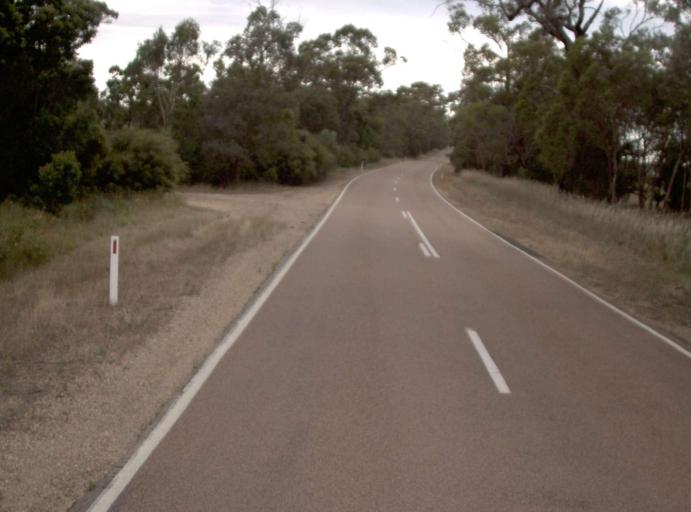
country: AU
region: Victoria
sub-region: Wellington
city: Sale
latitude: -38.0049
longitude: 147.2869
